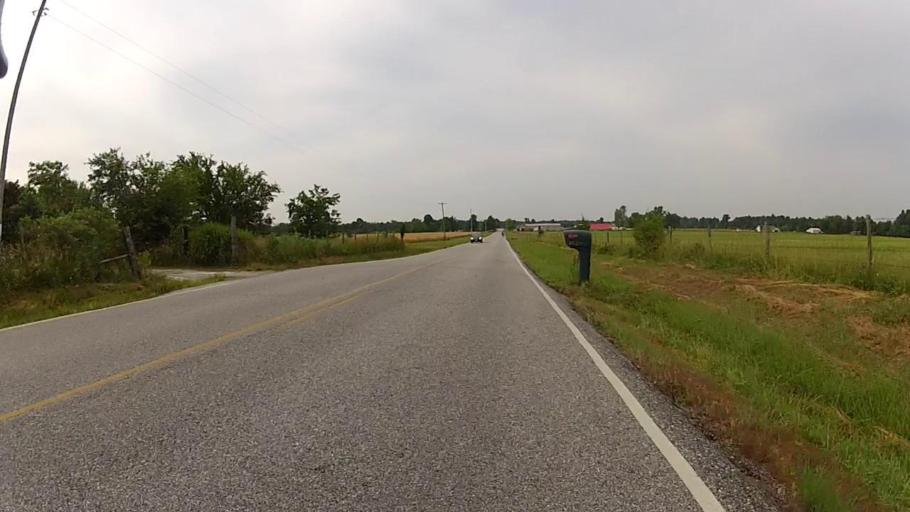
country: US
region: Kansas
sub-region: Cherokee County
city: Baxter Springs
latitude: 37.0781
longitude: -94.7223
